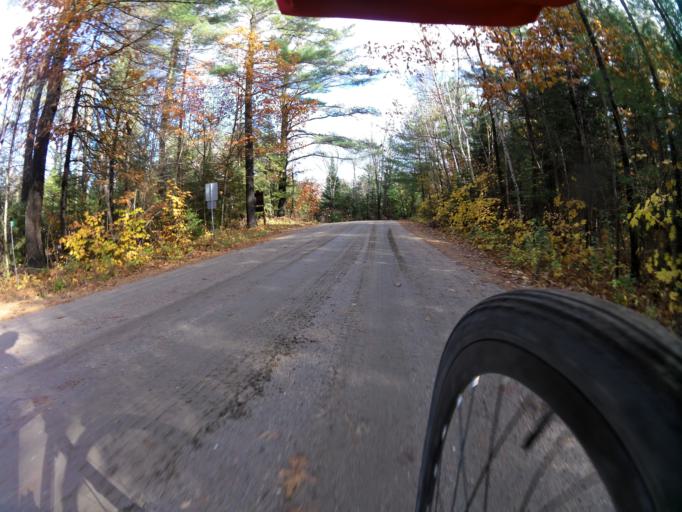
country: CA
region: Quebec
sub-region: Outaouais
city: Wakefield
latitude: 45.7261
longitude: -76.0269
